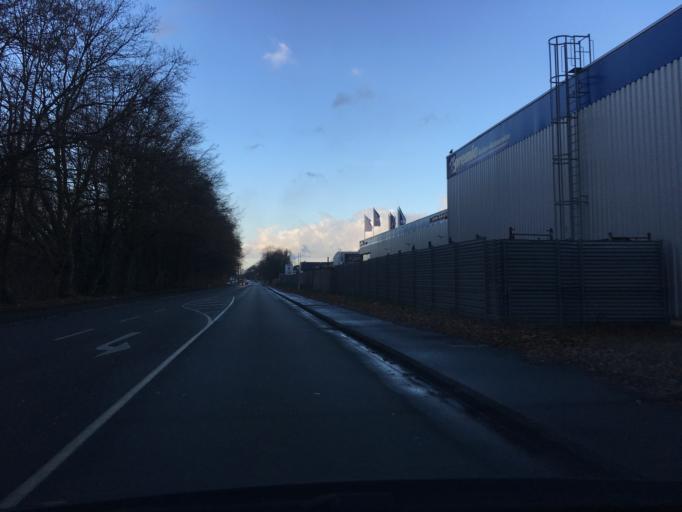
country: DE
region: North Rhine-Westphalia
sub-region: Regierungsbezirk Dusseldorf
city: Oberhausen
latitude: 51.4639
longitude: 6.8804
